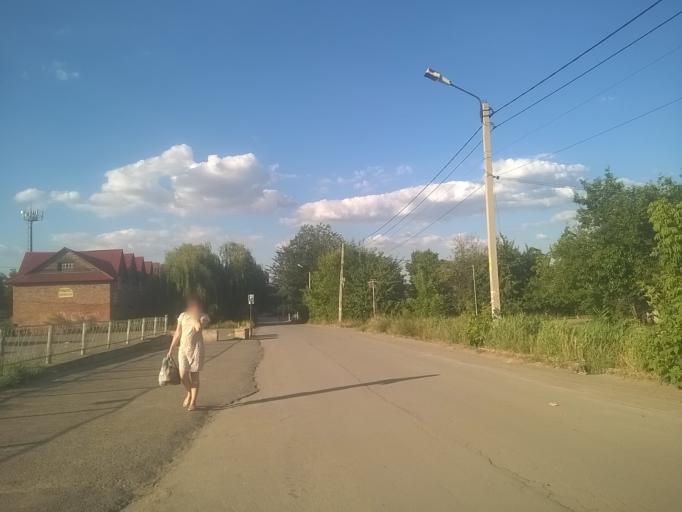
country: RU
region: Rostov
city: Donetsk
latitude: 48.3359
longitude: 39.9531
